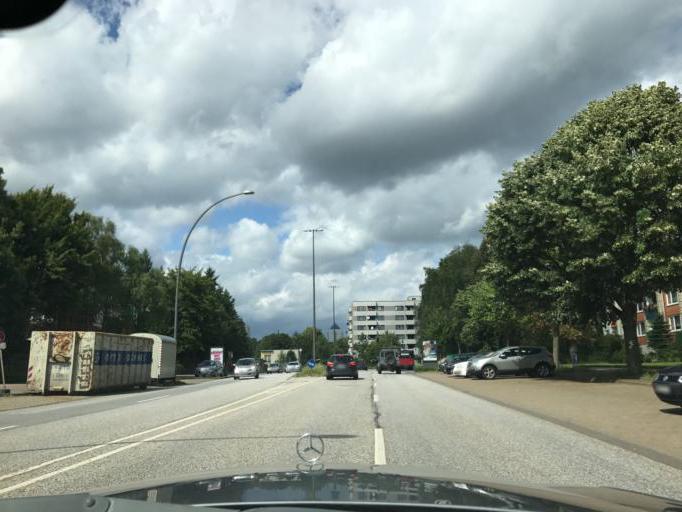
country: DE
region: Hamburg
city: Bergedorf
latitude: 53.5024
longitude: 10.2106
